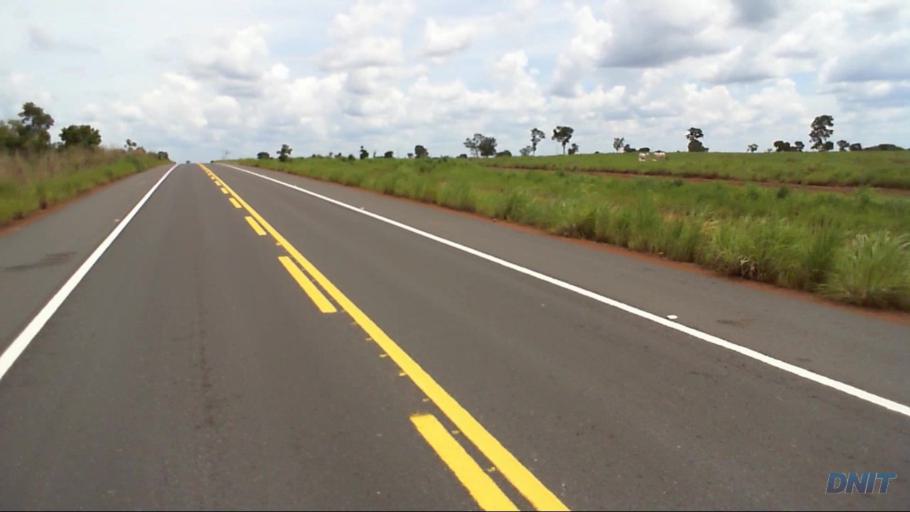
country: BR
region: Goias
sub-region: Sao Miguel Do Araguaia
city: Sao Miguel do Araguaia
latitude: -13.2693
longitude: -50.5077
